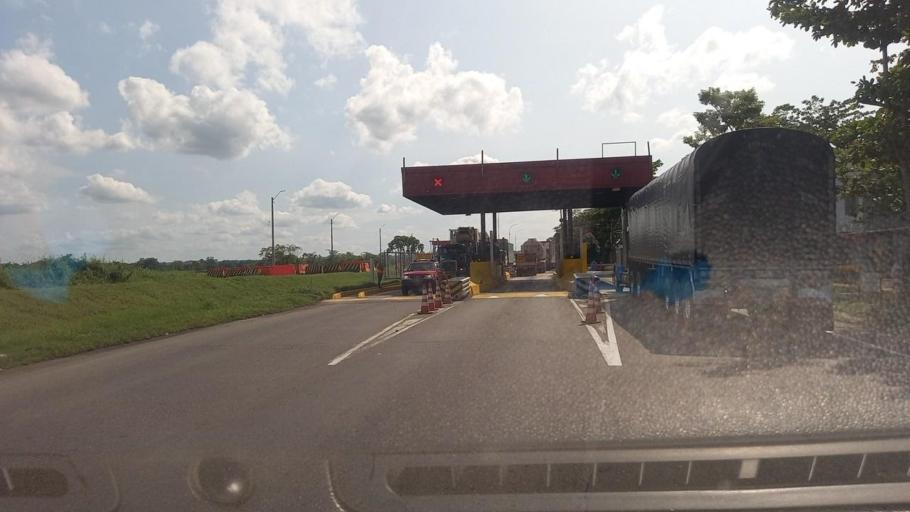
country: CO
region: Antioquia
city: Puerto Berrio
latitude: 6.2951
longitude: -74.4568
